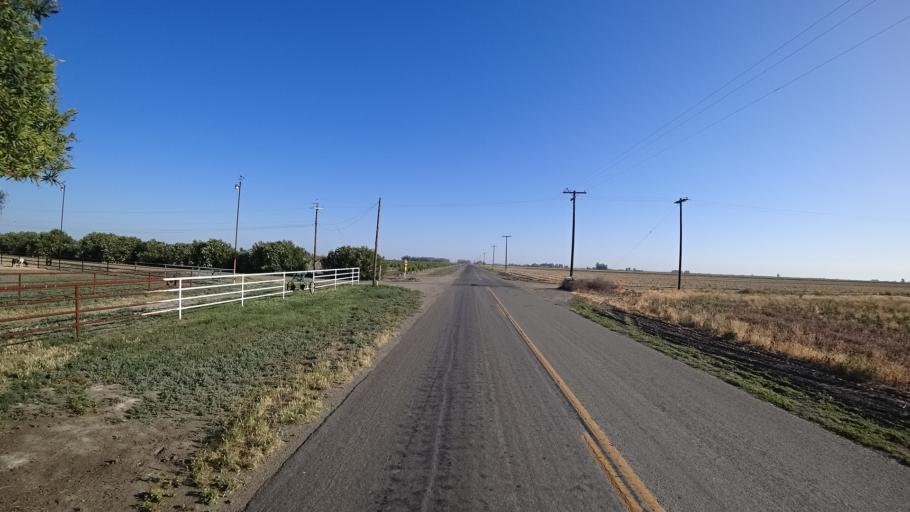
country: US
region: California
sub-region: Kings County
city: Stratford
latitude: 36.1745
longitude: -119.7982
